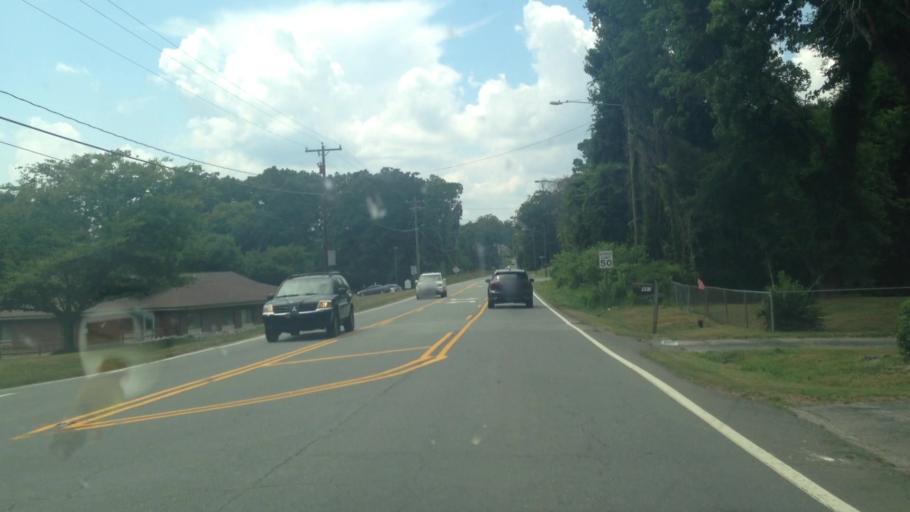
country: US
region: North Carolina
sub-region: Forsyth County
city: Rural Hall
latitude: 36.1956
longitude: -80.2609
